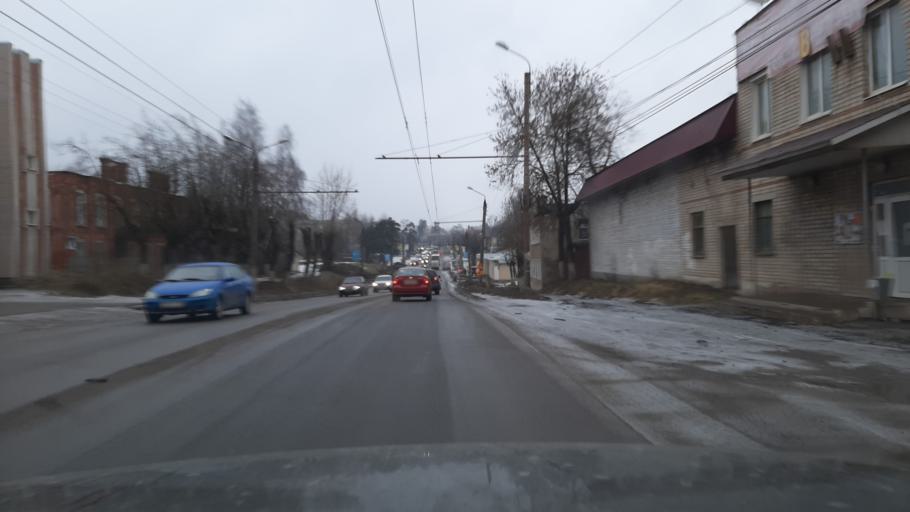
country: RU
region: Ivanovo
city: Kokhma
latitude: 56.9306
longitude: 41.0811
